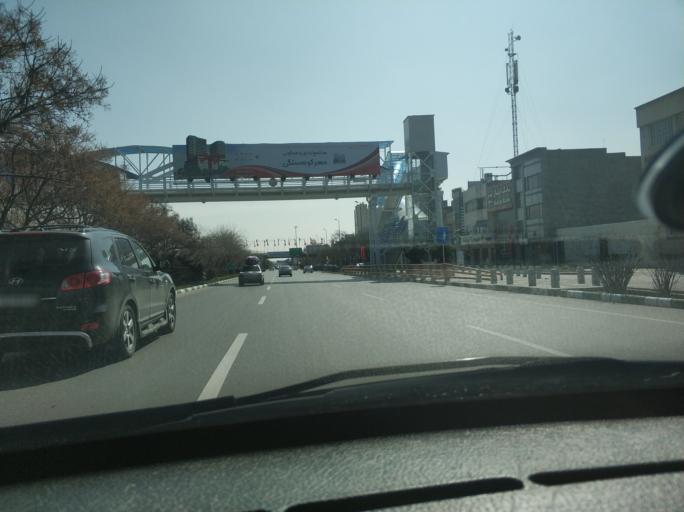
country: IR
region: Razavi Khorasan
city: Mashhad
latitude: 36.3238
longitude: 59.5123
